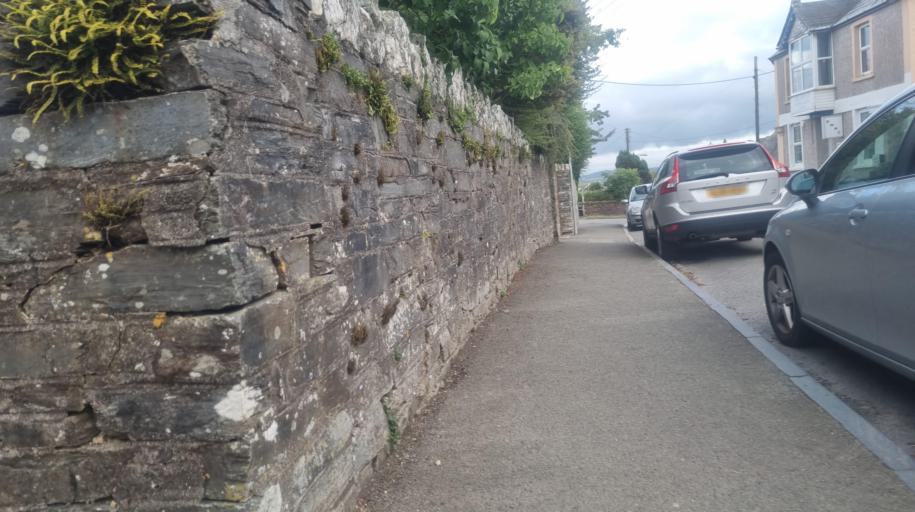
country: GB
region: England
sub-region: Cornwall
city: Tintagel
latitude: 50.6223
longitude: -4.7302
